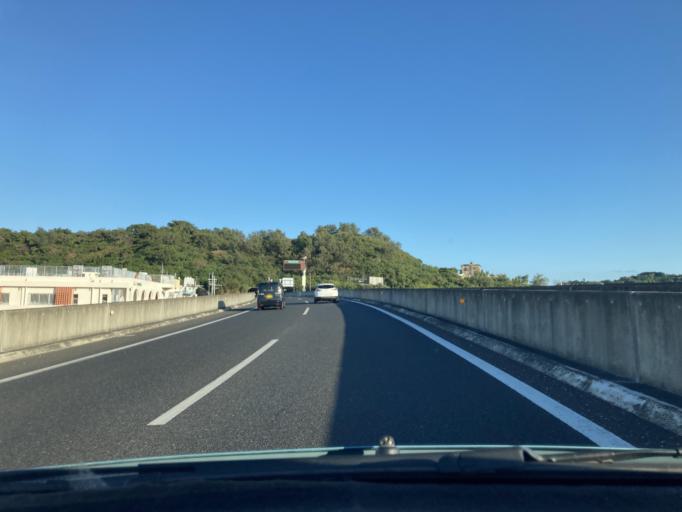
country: JP
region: Okinawa
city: Tomigusuku
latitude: 26.1719
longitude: 127.6776
